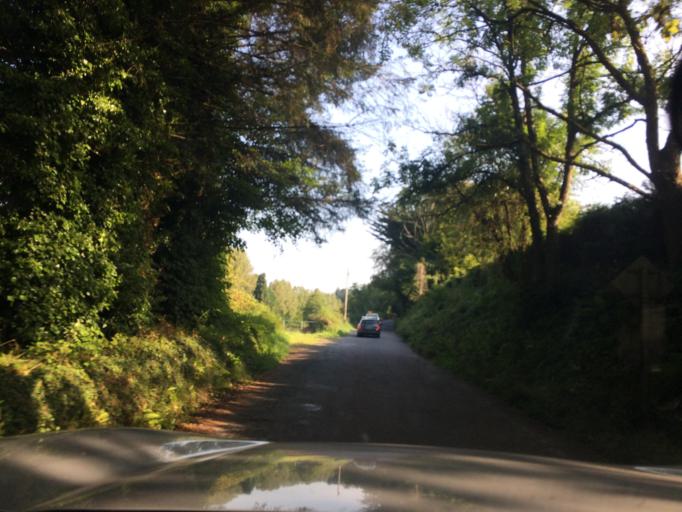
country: IE
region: Munster
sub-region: Waterford
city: Dungarvan
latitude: 52.1341
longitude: -7.6787
